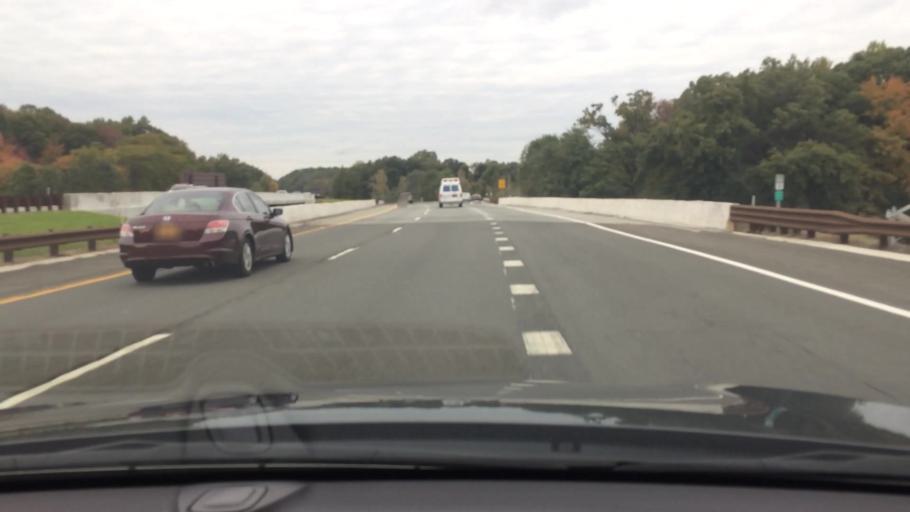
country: US
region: New York
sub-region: Rockland County
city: Bardonia
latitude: 41.1012
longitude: -73.9923
